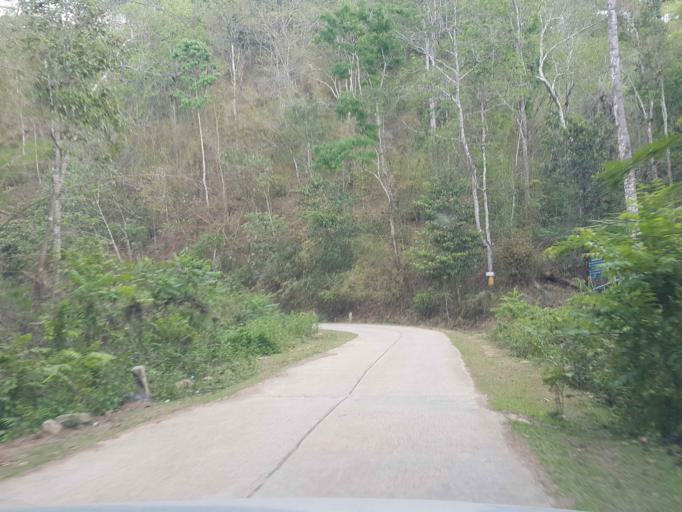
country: TH
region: Chiang Mai
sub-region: Amphoe Chiang Dao
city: Chiang Dao
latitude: 19.3749
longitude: 98.7560
